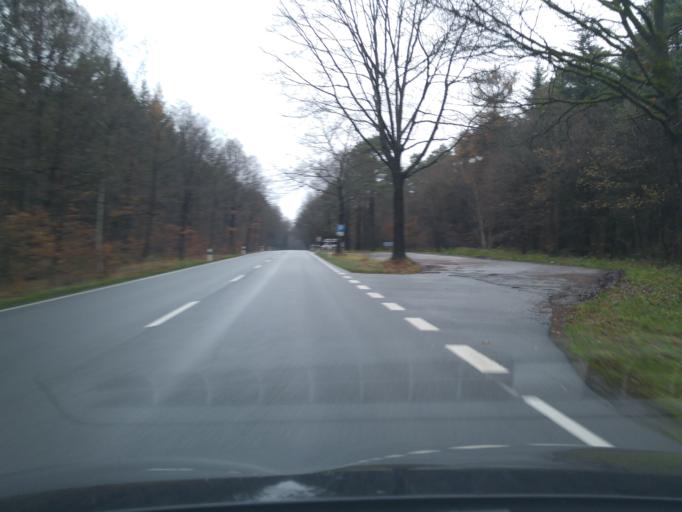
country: DE
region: Lower Saxony
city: Sprakensehl
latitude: 52.8062
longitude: 10.4876
